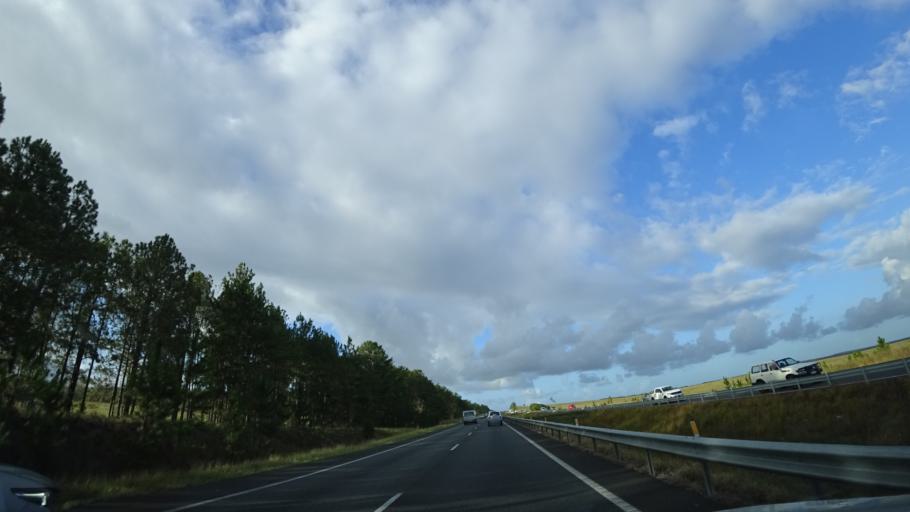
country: AU
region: Queensland
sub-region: Sunshine Coast
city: Little Mountain
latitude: -26.8307
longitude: 153.0336
